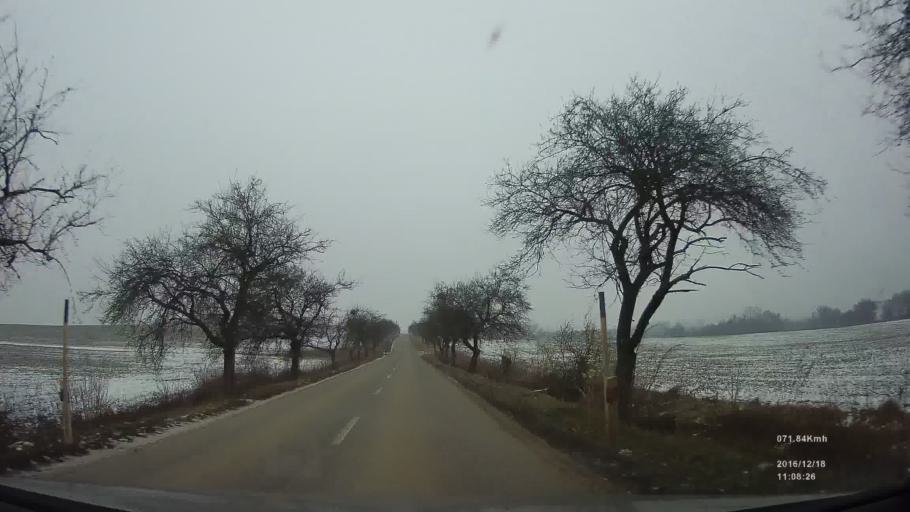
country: SK
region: Kosicky
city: Kosice
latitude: 48.8360
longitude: 21.3135
